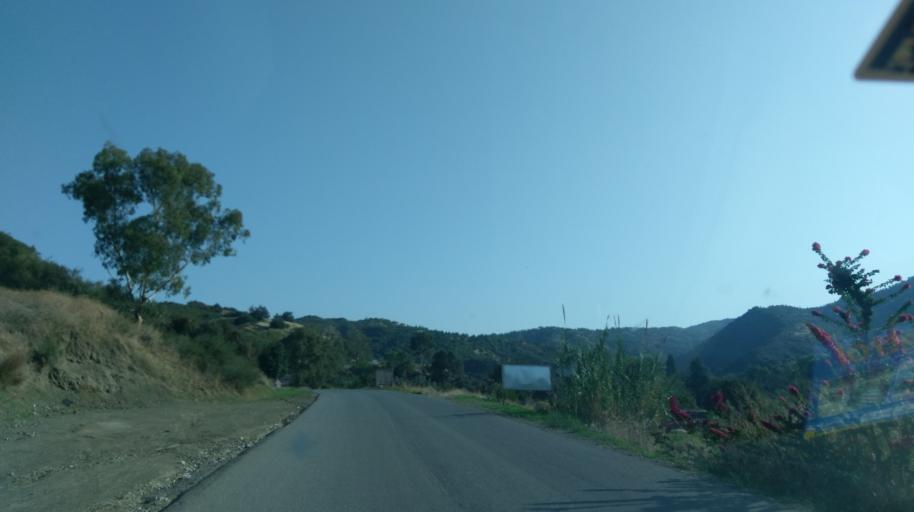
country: CY
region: Lefkosia
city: Kato Pyrgos
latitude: 35.1658
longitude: 32.7476
